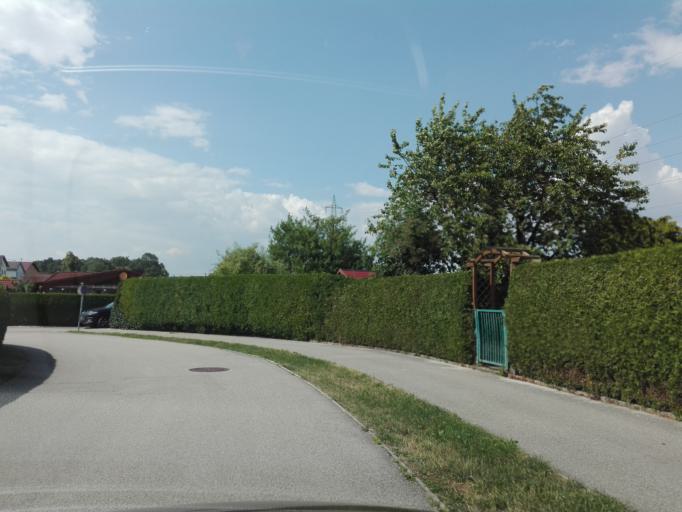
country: AT
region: Upper Austria
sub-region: Politischer Bezirk Linz-Land
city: Traun
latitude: 48.2139
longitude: 14.2135
